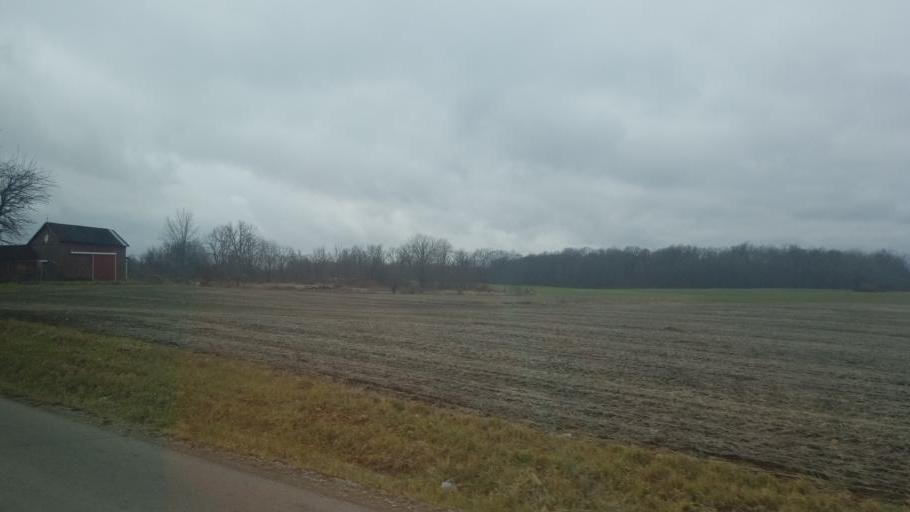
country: US
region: Ohio
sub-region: Crawford County
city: Galion
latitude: 40.7292
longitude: -82.8203
